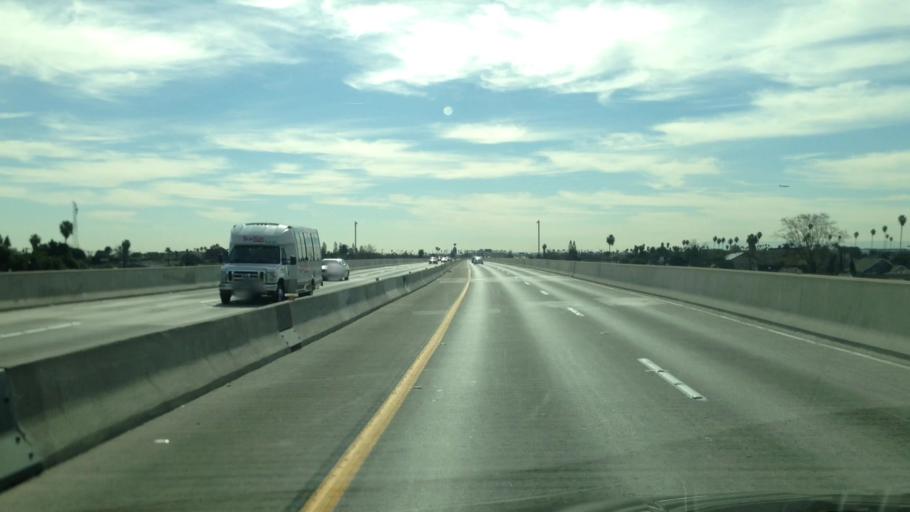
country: US
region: California
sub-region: Los Angeles County
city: Florence-Graham
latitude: 34.0022
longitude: -118.2811
